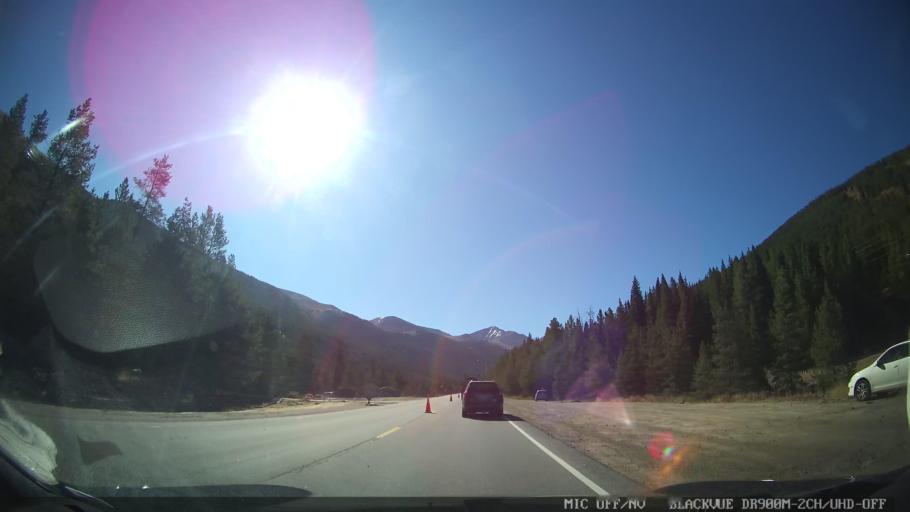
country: US
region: Colorado
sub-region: Summit County
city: Frisco
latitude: 39.4933
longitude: -106.1363
